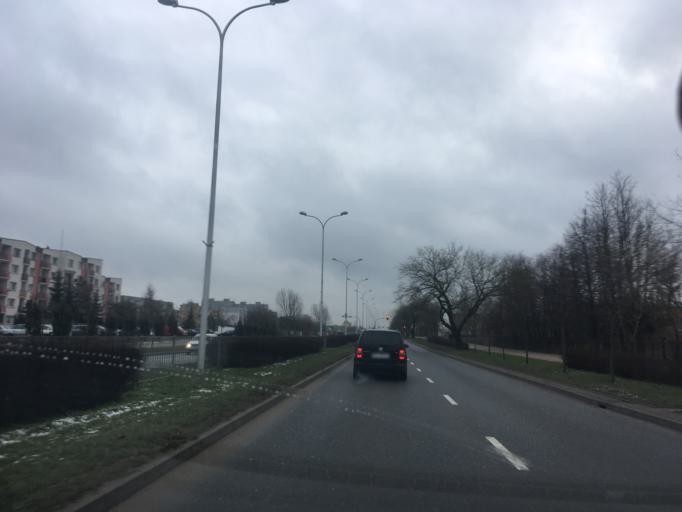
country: PL
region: Podlasie
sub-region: Suwalki
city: Suwalki
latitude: 54.1229
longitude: 22.9295
